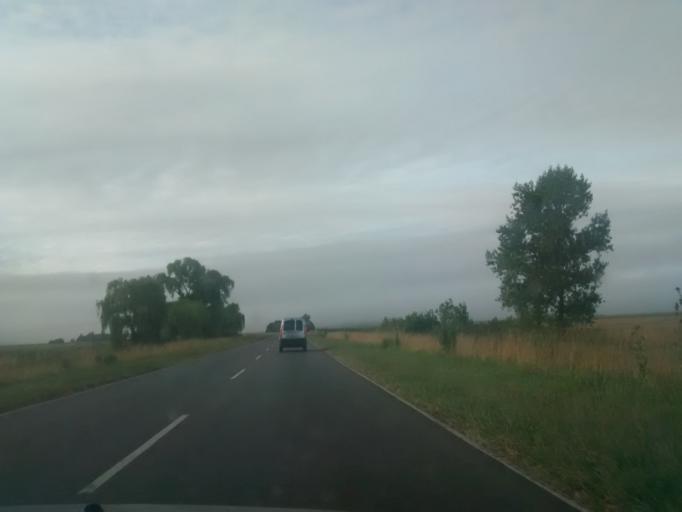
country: AR
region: Buenos Aires
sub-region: Partido de Brandsen
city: Brandsen
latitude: -35.3397
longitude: -58.2453
